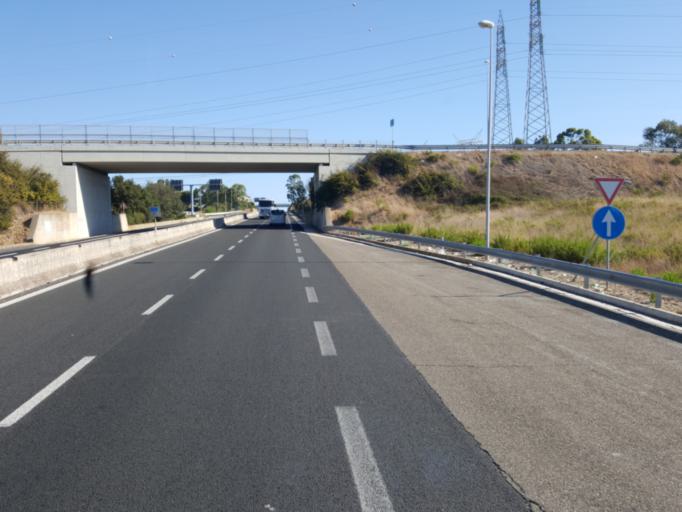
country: IT
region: Latium
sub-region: Citta metropolitana di Roma Capitale
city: Aurelia
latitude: 42.1285
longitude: 11.7924
